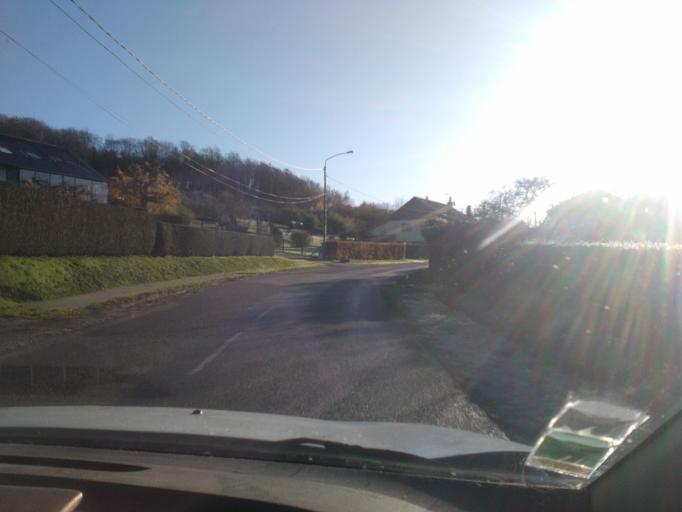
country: FR
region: Lorraine
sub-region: Departement des Vosges
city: Xertigny
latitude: 48.0525
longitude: 6.3749
